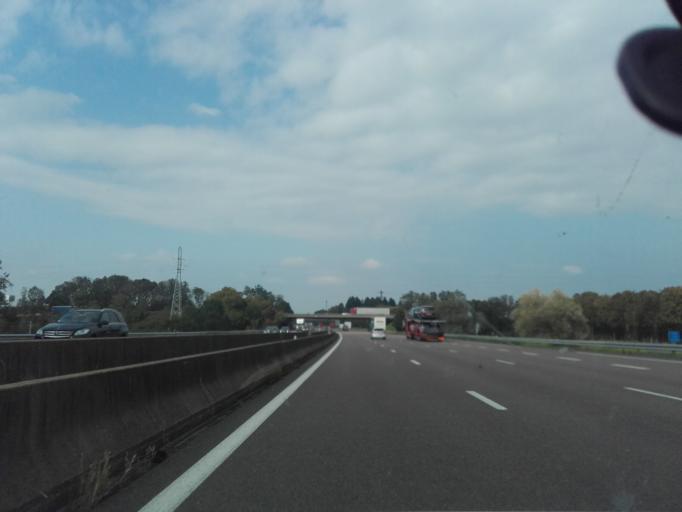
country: FR
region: Bourgogne
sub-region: Departement de Saone-et-Loire
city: Saint-Remy
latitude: 46.7541
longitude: 4.8309
